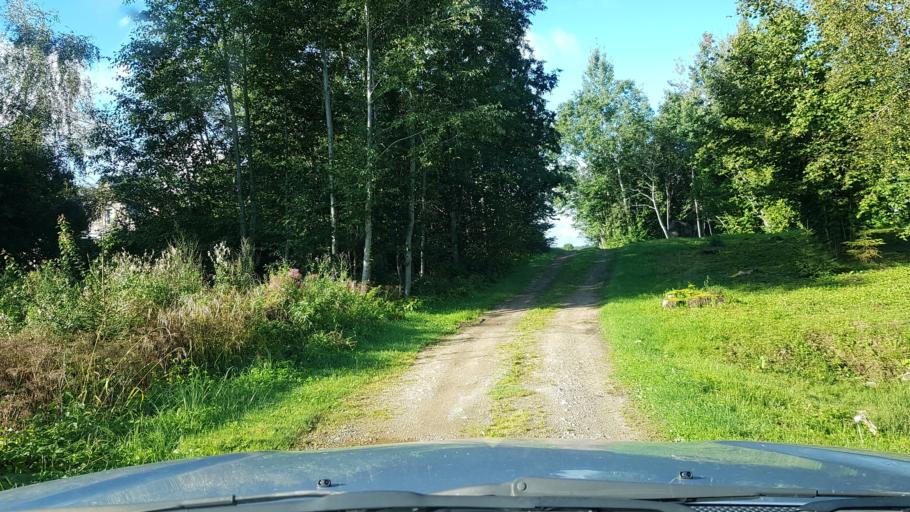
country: EE
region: Harju
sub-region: Rae vald
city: Vaida
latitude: 59.2544
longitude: 25.0281
